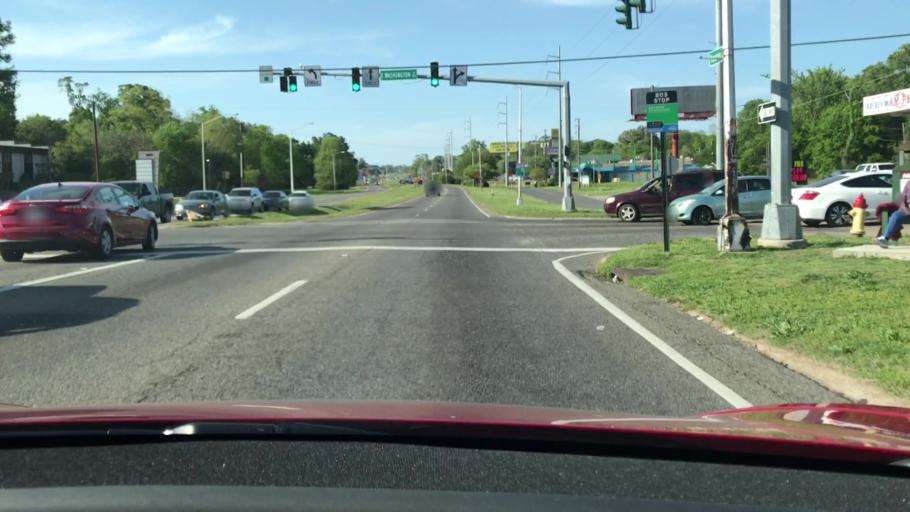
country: US
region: Louisiana
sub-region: Bossier Parish
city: Bossier City
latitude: 32.4846
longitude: -93.7240
